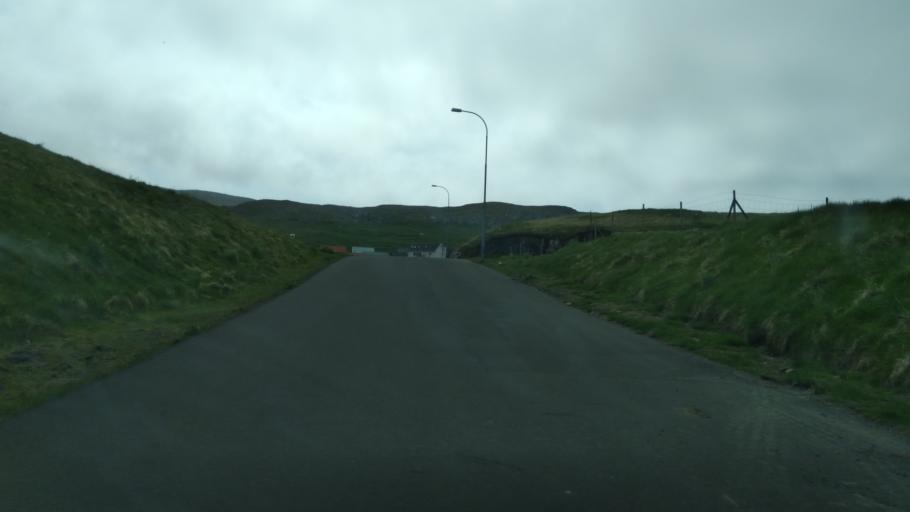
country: FO
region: Sandoy
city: Sandur
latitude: 61.9053
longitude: -6.8854
